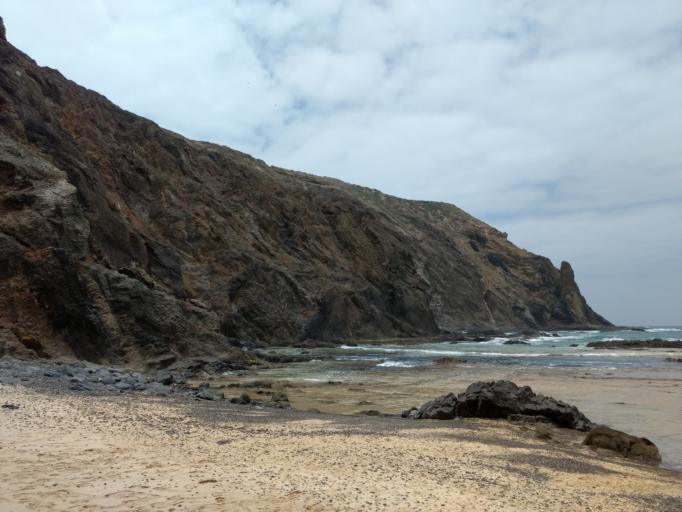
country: PT
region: Madeira
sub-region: Porto Santo
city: Camacha
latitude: 33.0932
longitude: -16.3472
